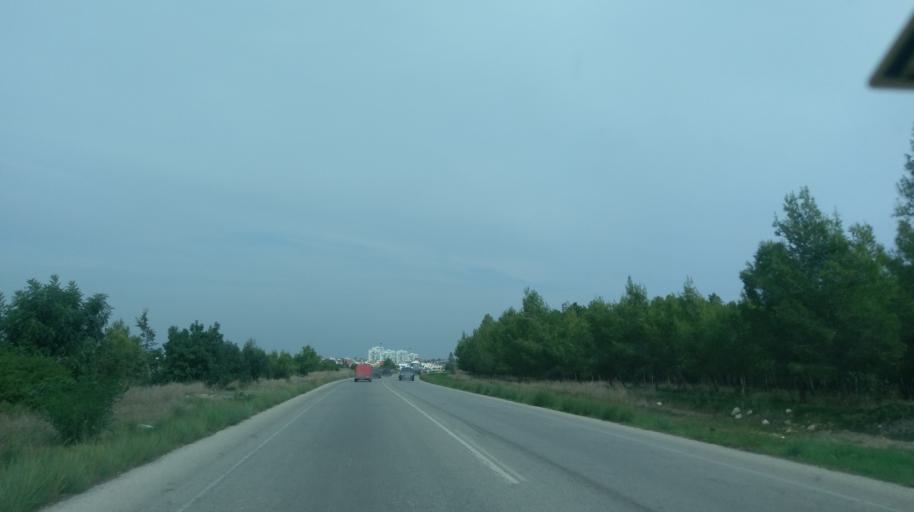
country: CY
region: Ammochostos
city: Trikomo
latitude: 35.2942
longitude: 33.9335
